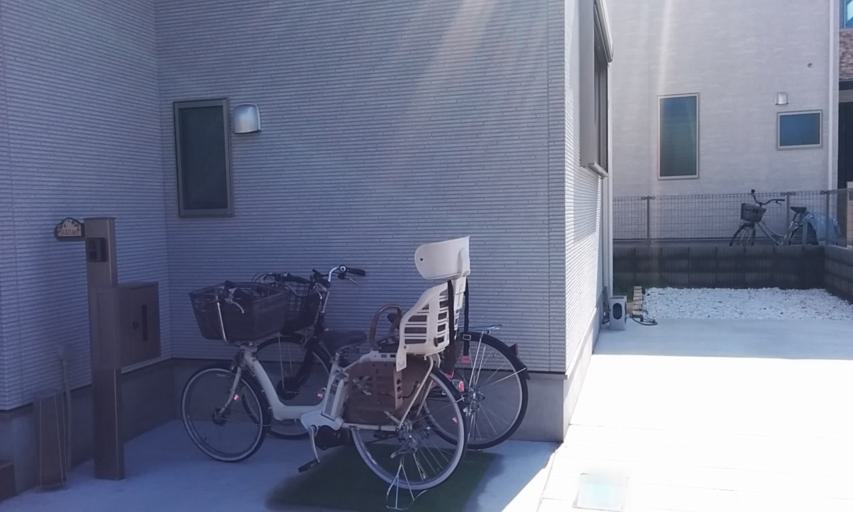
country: JP
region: Tokyo
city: Kokubunji
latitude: 35.6956
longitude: 139.4791
